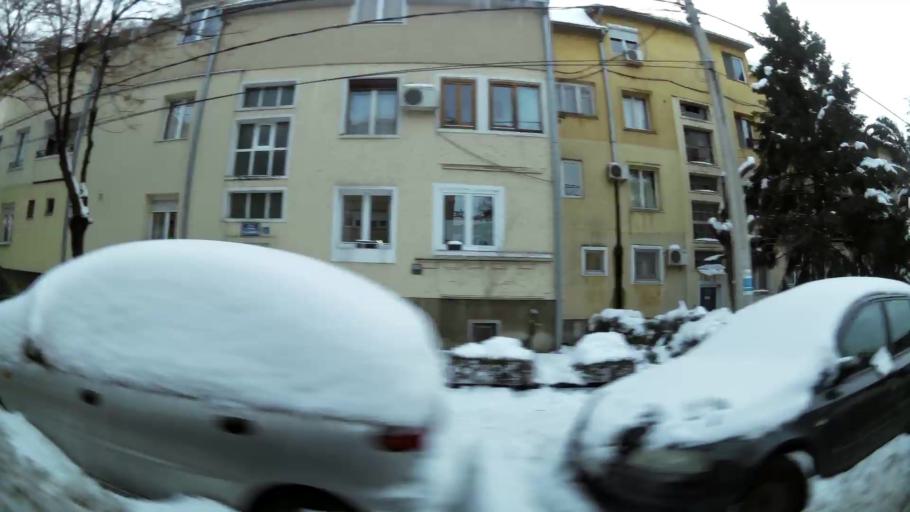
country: RS
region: Central Serbia
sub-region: Belgrade
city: Palilula
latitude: 44.7942
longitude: 20.5059
